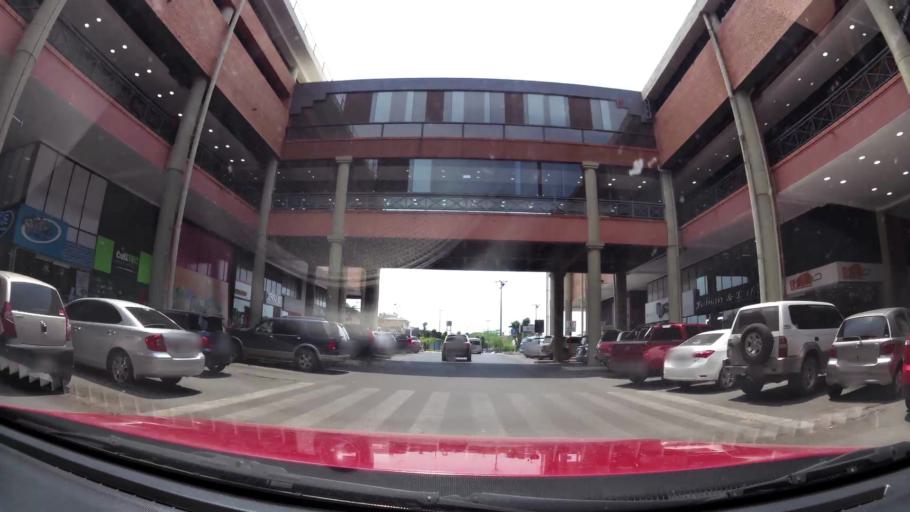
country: PY
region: Central
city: Lambare
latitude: -25.3168
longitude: -57.5709
